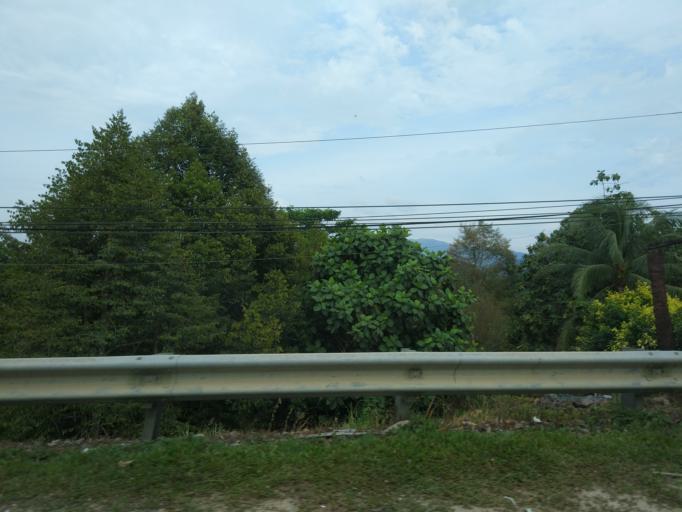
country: MY
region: Sabah
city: Beaufort
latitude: 5.0606
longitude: 115.5506
